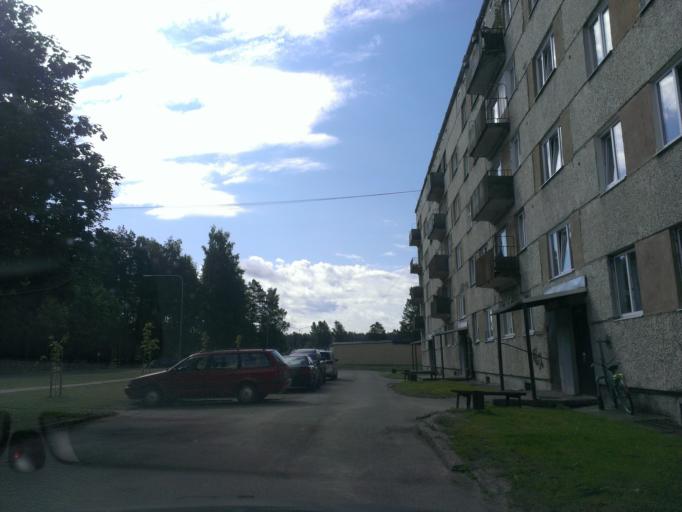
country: LV
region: Incukalns
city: Vangazi
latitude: 57.0897
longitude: 24.5445
